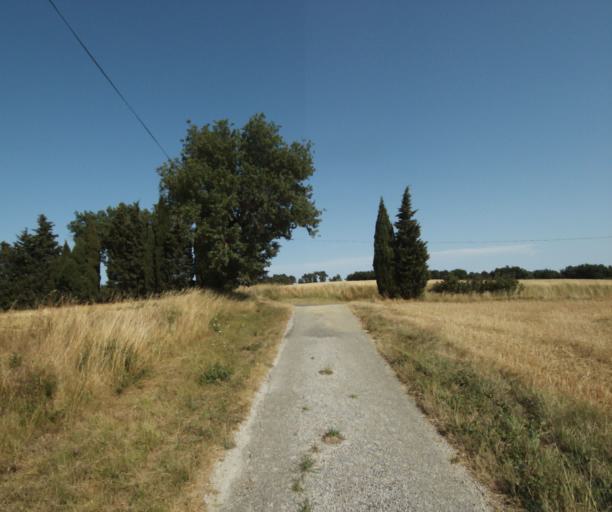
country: FR
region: Midi-Pyrenees
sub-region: Departement de la Haute-Garonne
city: Saint-Felix-Lauragais
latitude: 43.4270
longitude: 1.8453
